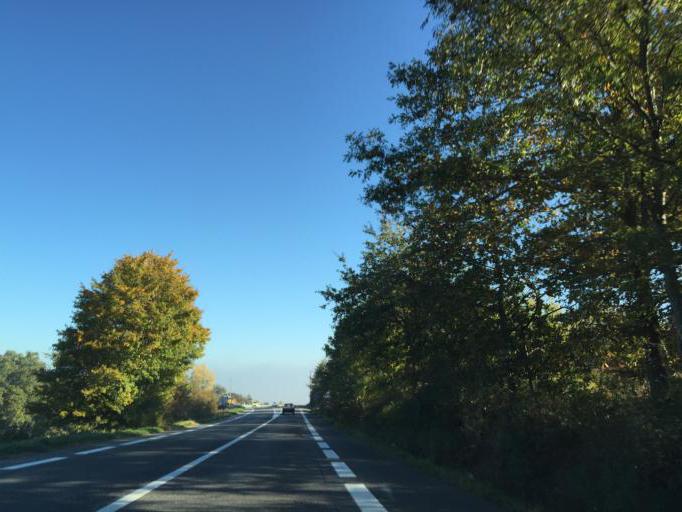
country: FR
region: Rhone-Alpes
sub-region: Departement du Rhone
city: Taluyers
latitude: 45.6425
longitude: 4.7421
